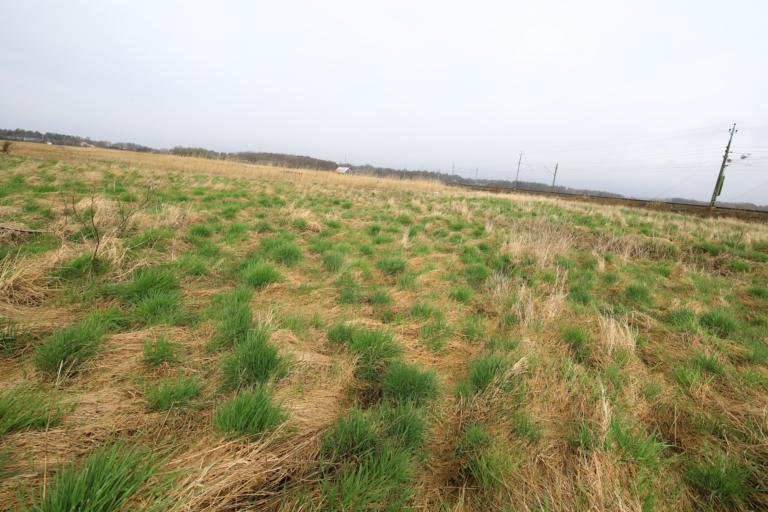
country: SE
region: Halland
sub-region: Kungsbacka Kommun
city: Frillesas
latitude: 57.3074
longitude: 12.1695
